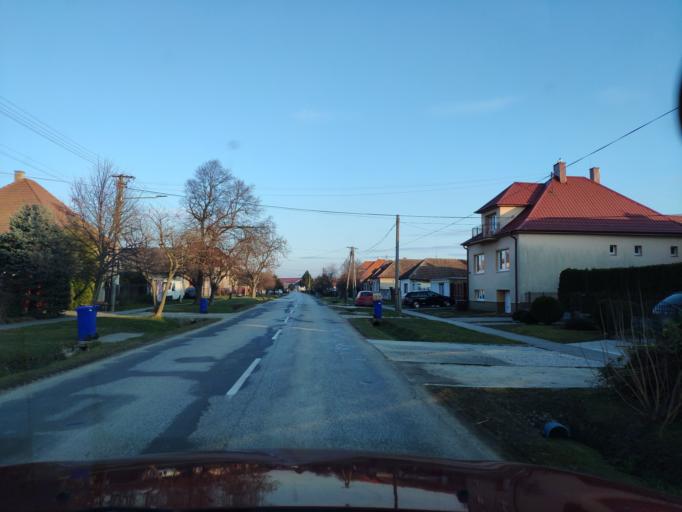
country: SK
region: Nitriansky
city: Sellye
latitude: 48.2573
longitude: 17.8625
